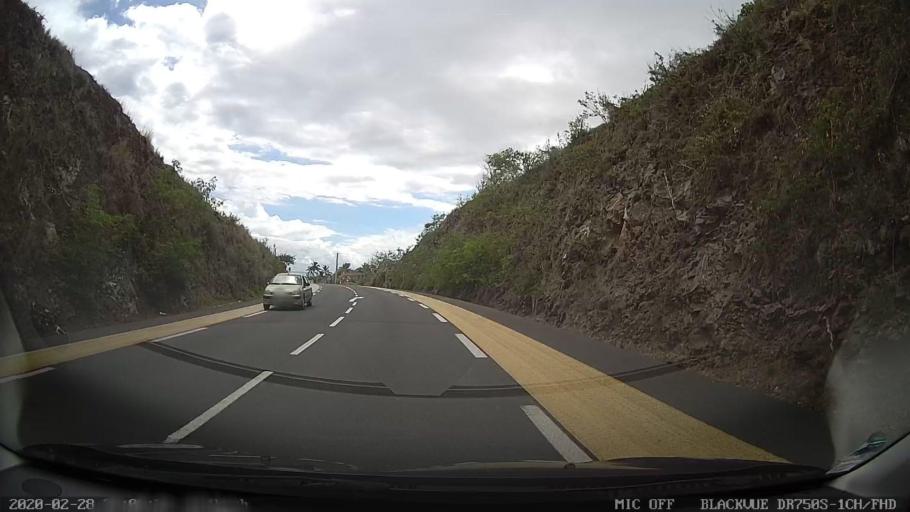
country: RE
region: Reunion
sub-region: Reunion
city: Trois-Bassins
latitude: -21.1241
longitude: 55.2657
